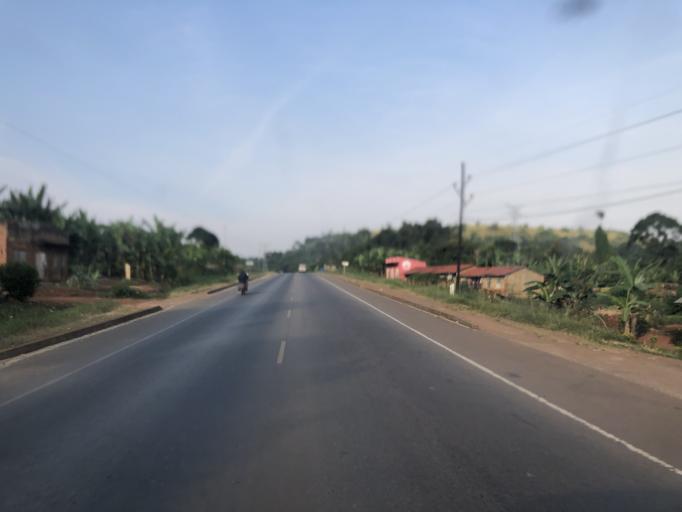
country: UG
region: Central Region
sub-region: Mpigi District
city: Mpigi
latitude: 0.1729
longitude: 32.2703
